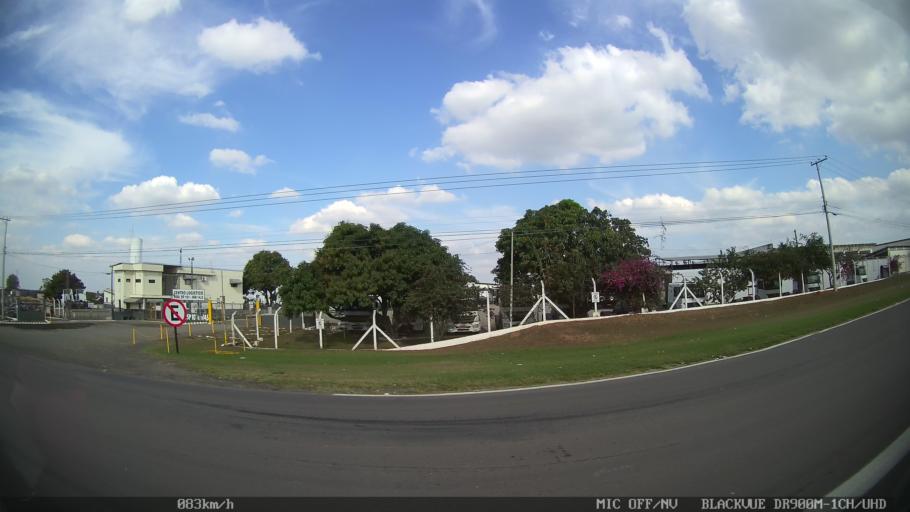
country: BR
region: Sao Paulo
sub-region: Hortolandia
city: Hortolandia
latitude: -22.9082
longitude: -47.2394
